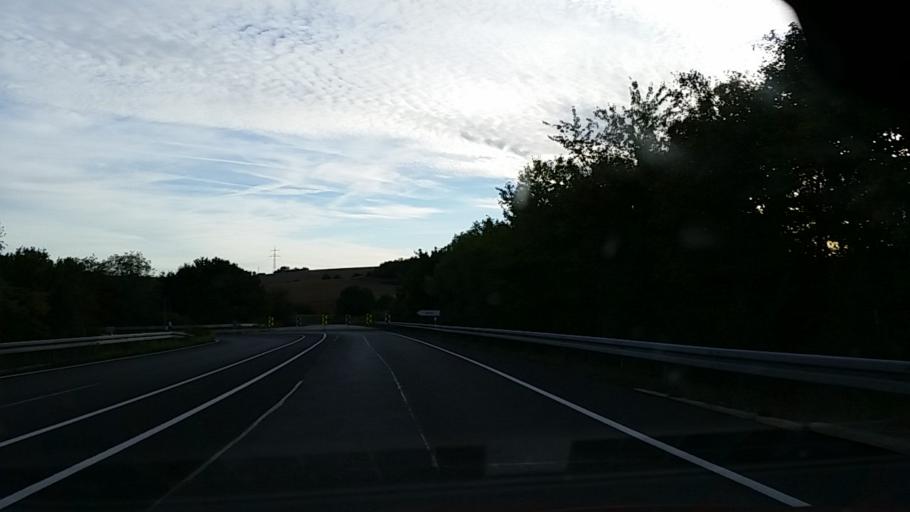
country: DE
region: Bavaria
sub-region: Regierungsbezirk Unterfranken
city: Arnstein
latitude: 49.9949
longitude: 9.9846
